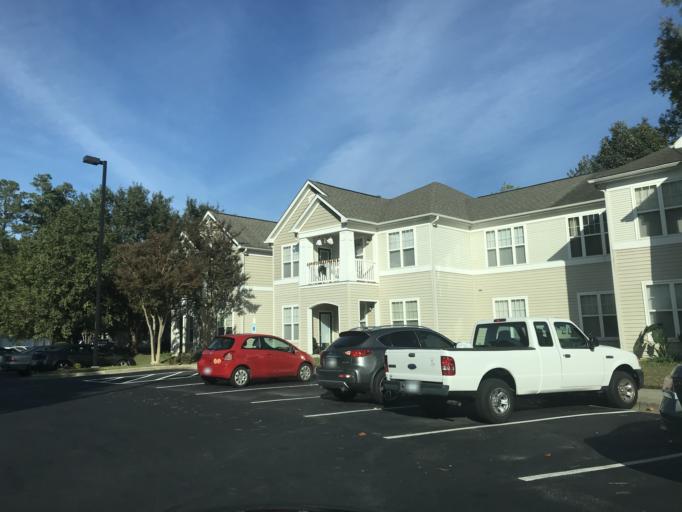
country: US
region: North Carolina
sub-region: Wake County
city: Wake Forest
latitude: 35.9011
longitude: -78.5527
